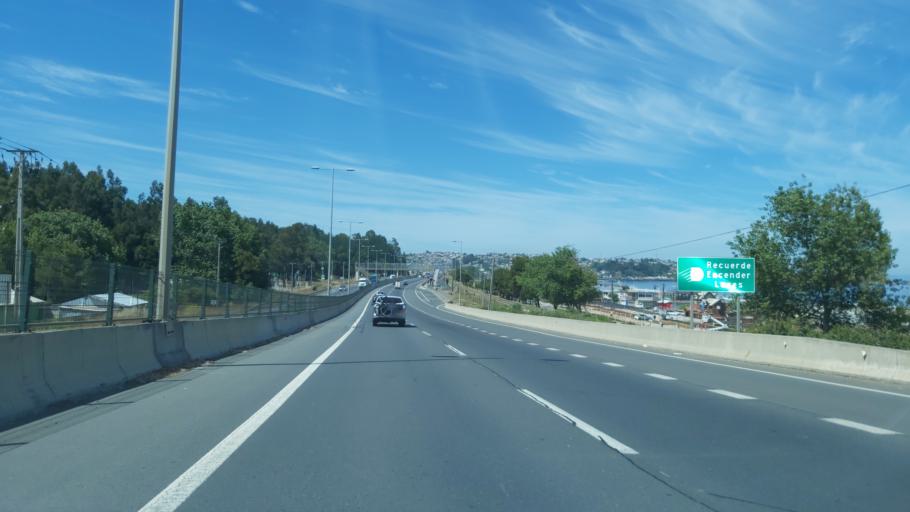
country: CL
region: Biobio
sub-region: Provincia de Concepcion
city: Coronel
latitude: -37.0605
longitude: -73.1405
